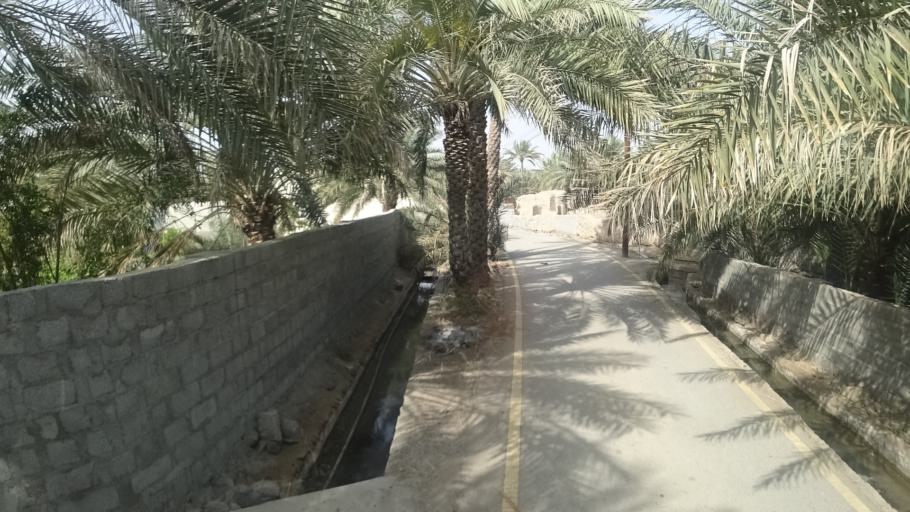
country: OM
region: Ash Sharqiyah
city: Ibra'
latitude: 22.7116
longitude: 58.1714
